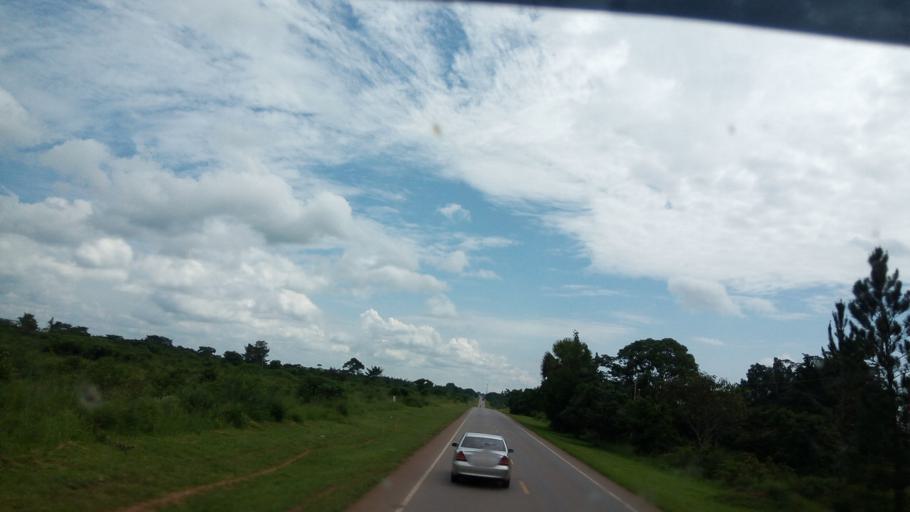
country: UG
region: Central Region
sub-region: Nakasongola District
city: Nakasongola
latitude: 1.2245
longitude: 32.4648
